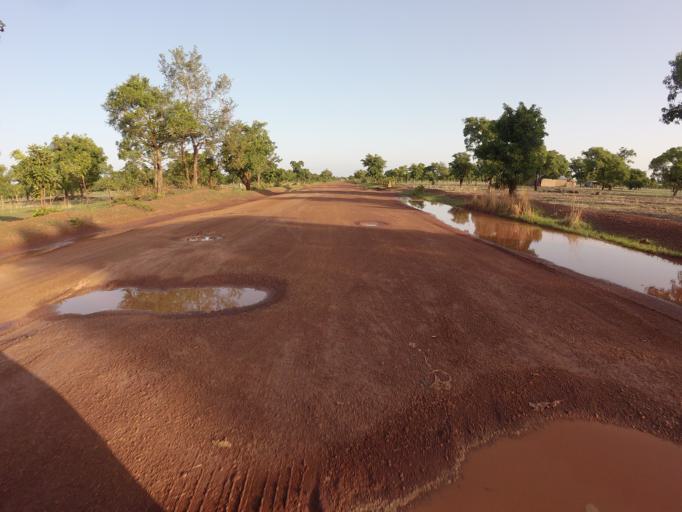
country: TG
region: Savanes
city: Sansanne-Mango
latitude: 10.2771
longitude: -0.0833
